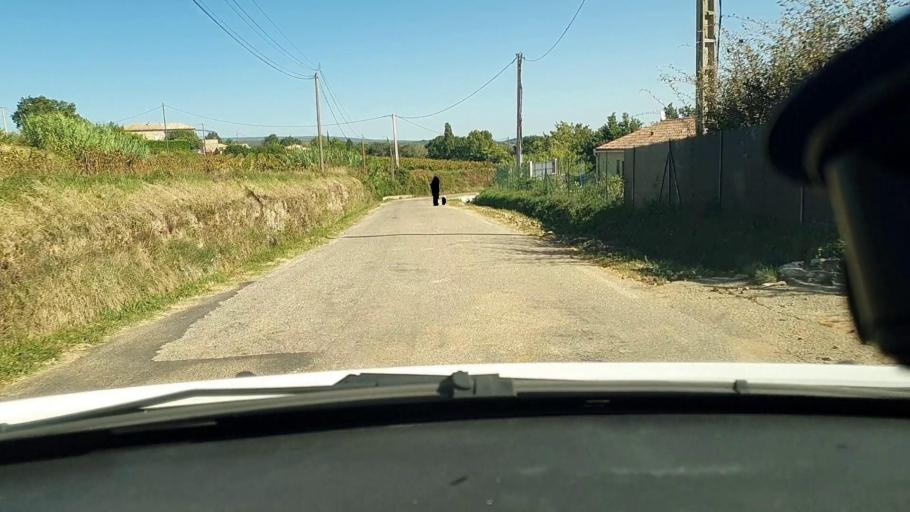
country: FR
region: Languedoc-Roussillon
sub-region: Departement du Gard
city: Saint-Julien-de-Peyrolas
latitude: 44.2818
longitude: 4.5597
